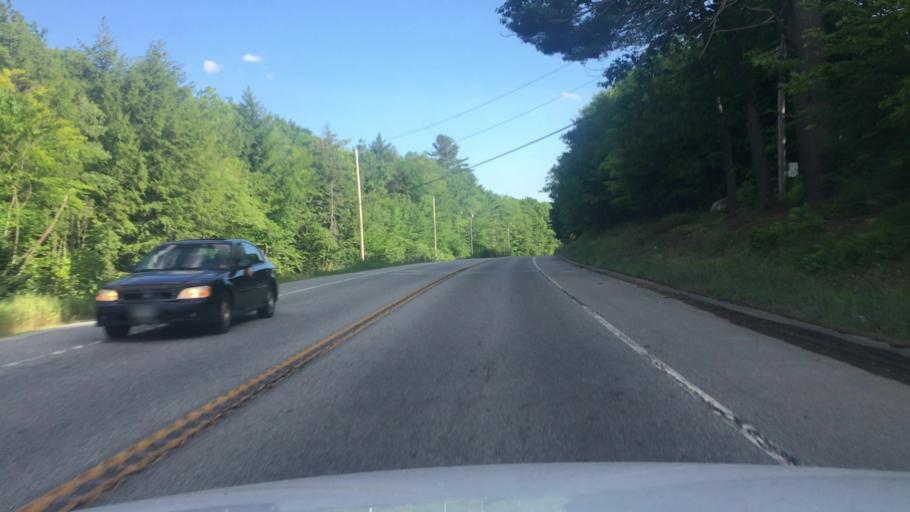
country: US
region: Maine
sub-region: Androscoggin County
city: Livermore
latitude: 44.4183
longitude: -70.2203
